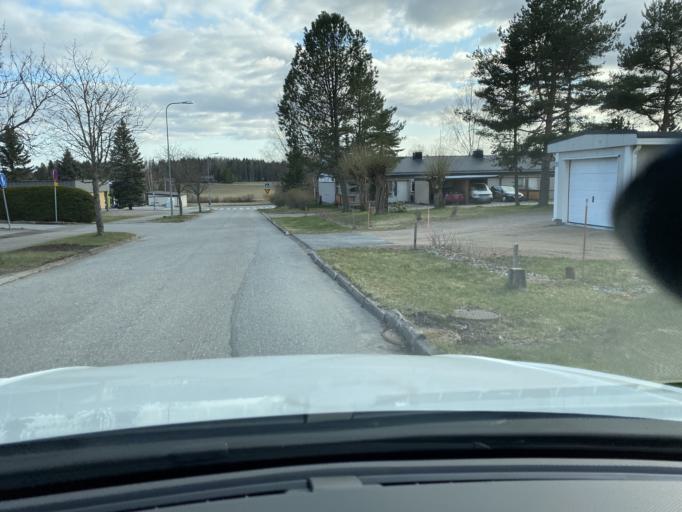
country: FI
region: Pirkanmaa
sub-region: Lounais-Pirkanmaa
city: Punkalaidun
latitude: 61.1136
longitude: 23.1026
